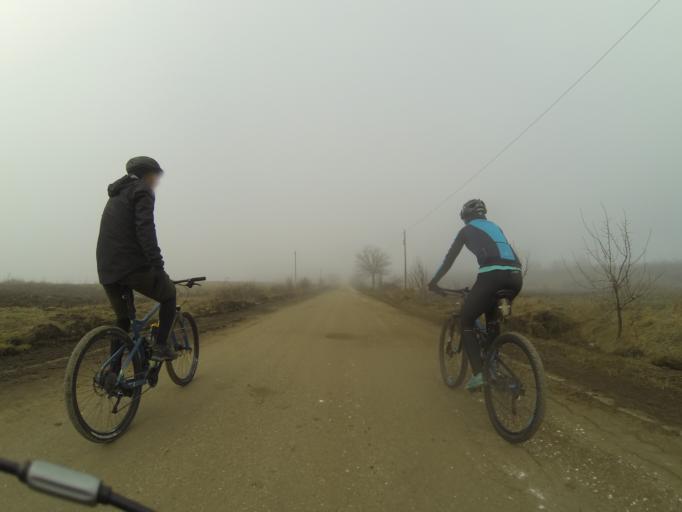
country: RO
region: Mehedinti
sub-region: Comuna Baclesu
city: Baclesu
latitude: 44.4852
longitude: 23.1015
